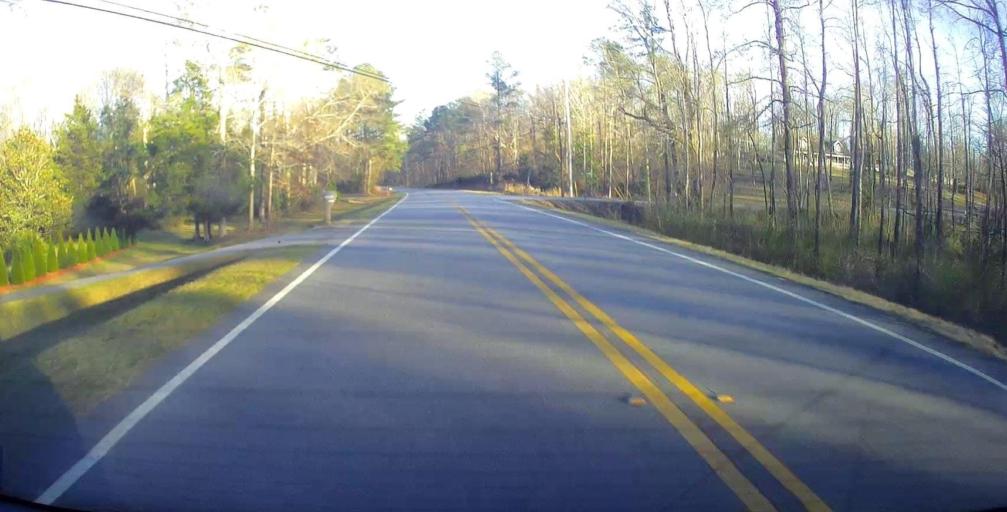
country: US
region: Georgia
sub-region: Harris County
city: Hamilton
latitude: 32.6302
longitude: -84.7990
